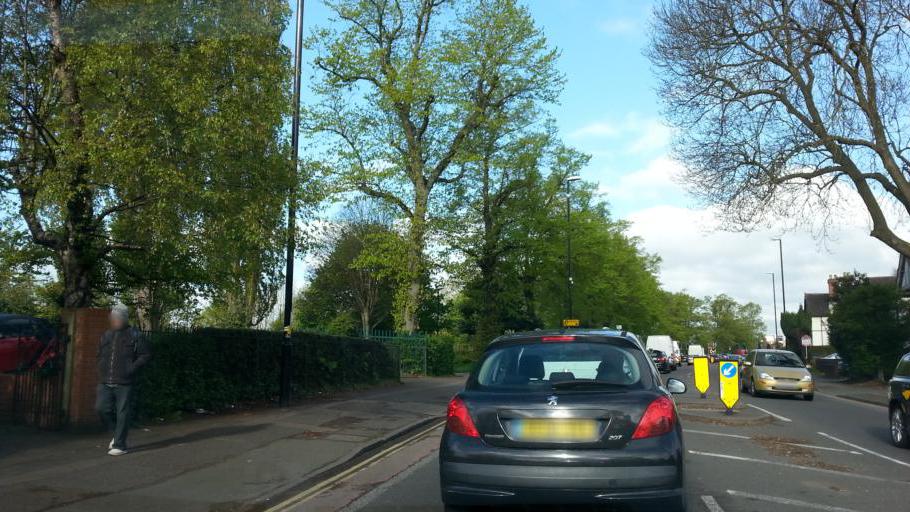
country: GB
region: England
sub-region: Coventry
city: Coventry
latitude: 52.4062
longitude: -1.4845
